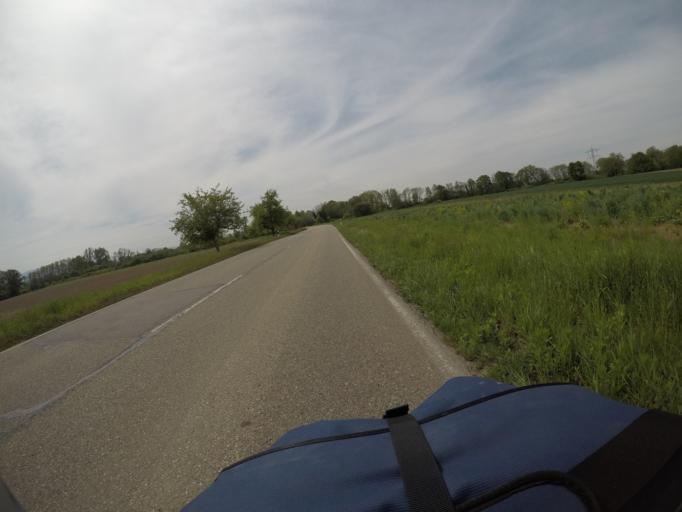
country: DE
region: Baden-Wuerttemberg
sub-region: Karlsruhe Region
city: Schwarzach
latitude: 48.7546
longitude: 8.0387
